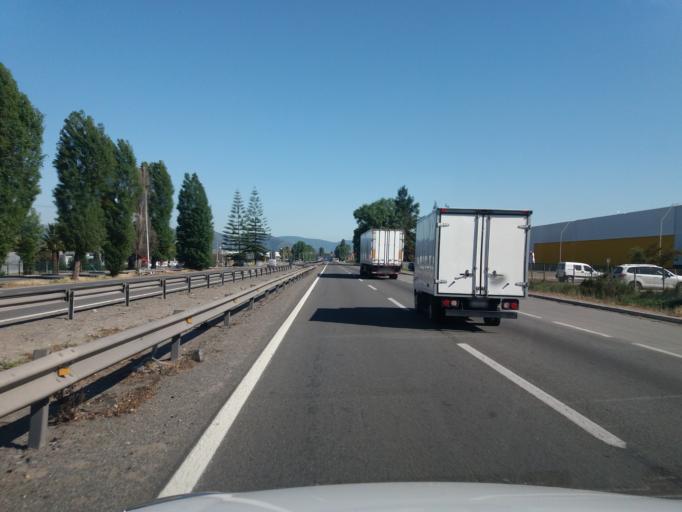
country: CL
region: Valparaiso
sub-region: Provincia de Quillota
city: Hacienda La Calera
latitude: -32.7994
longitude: -71.1572
